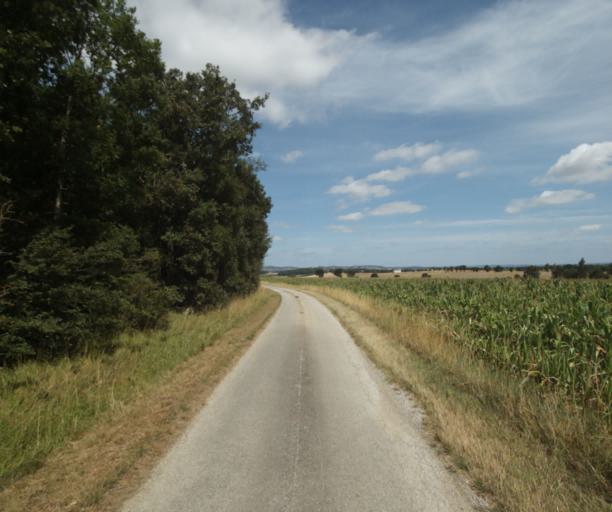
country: FR
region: Midi-Pyrenees
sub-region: Departement du Tarn
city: Dourgne
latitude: 43.4875
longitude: 2.1010
